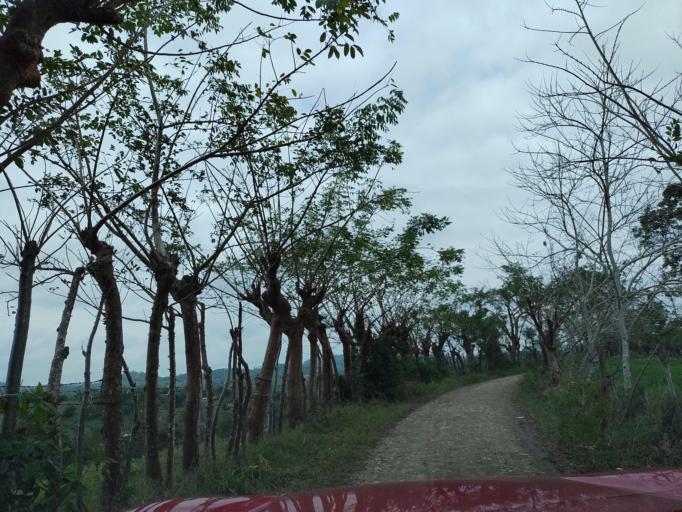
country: MX
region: Veracruz
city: Coatzintla
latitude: 20.4588
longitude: -97.4167
